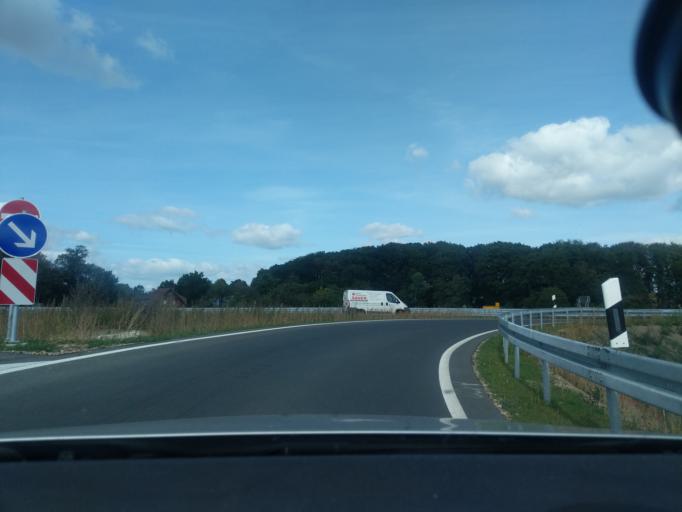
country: DE
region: Lower Saxony
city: Belm
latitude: 52.3069
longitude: 8.1187
